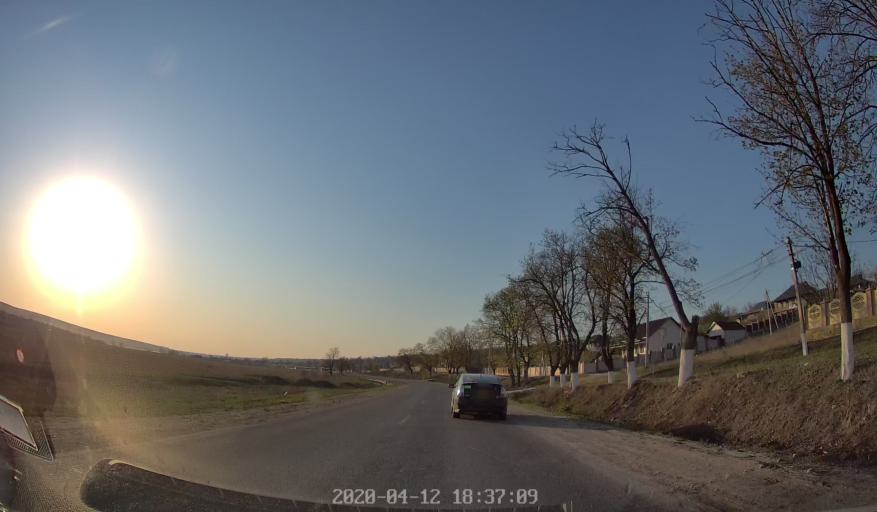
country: MD
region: Chisinau
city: Vadul lui Voda
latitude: 47.1191
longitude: 29.0193
